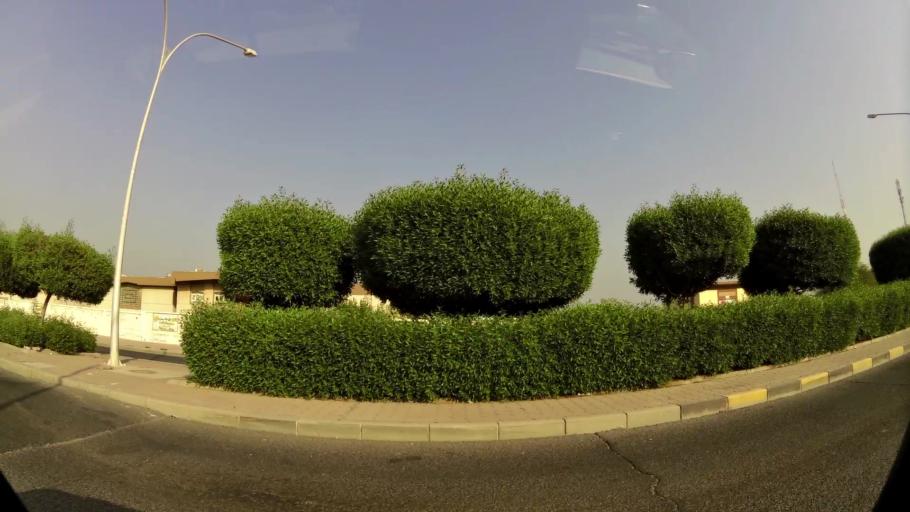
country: KW
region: Al Ahmadi
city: Al Manqaf
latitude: 29.1128
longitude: 48.1055
